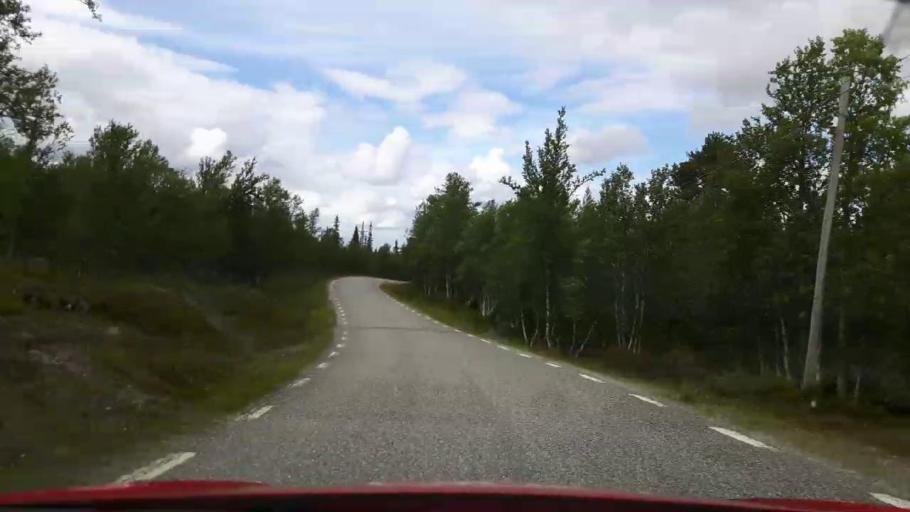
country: NO
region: Hedmark
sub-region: Engerdal
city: Engerdal
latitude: 62.3513
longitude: 12.7945
